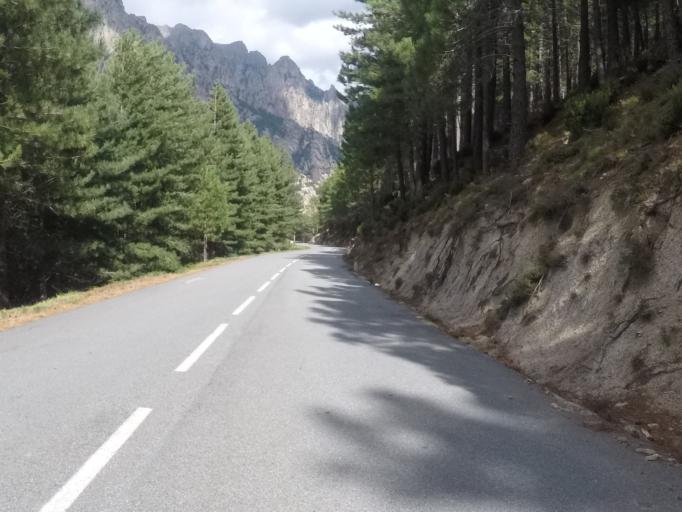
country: FR
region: Corsica
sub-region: Departement de la Corse-du-Sud
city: Zonza
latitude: 41.8005
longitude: 9.2371
